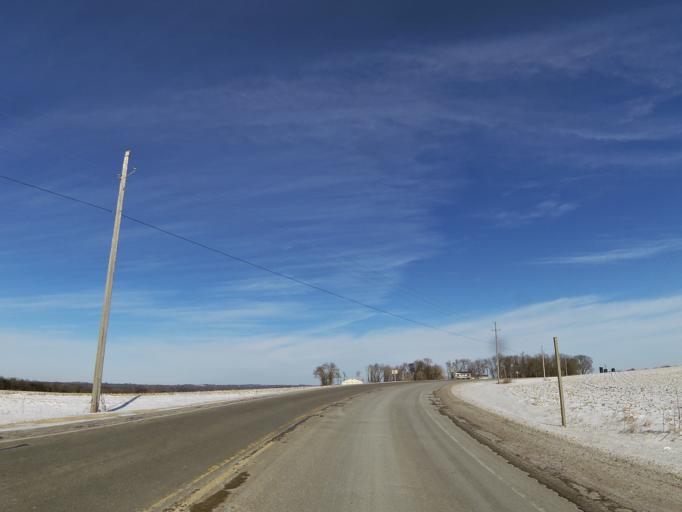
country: US
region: Wisconsin
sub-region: Pierce County
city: Prescott
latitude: 44.7762
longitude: -92.7778
